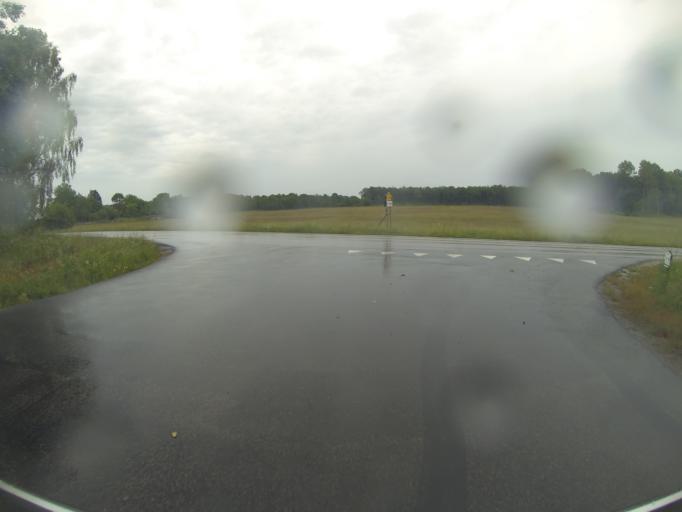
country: SE
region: Blekinge
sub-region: Ronneby Kommun
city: Ronneby
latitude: 56.1715
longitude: 15.3279
